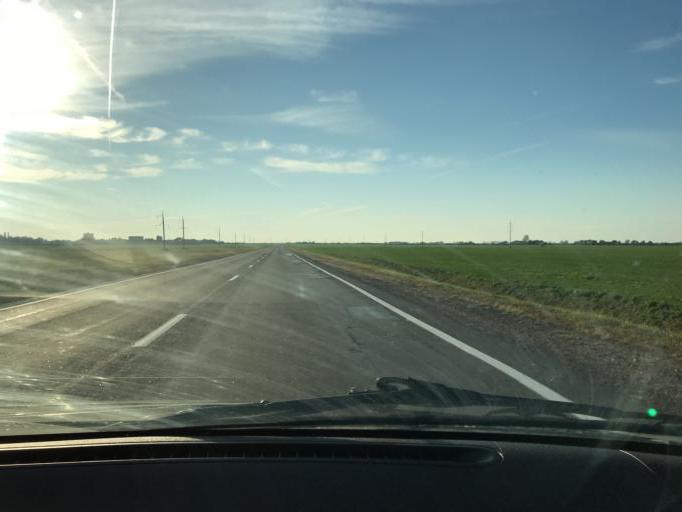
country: BY
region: Brest
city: Antopal'
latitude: 52.2218
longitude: 24.6996
